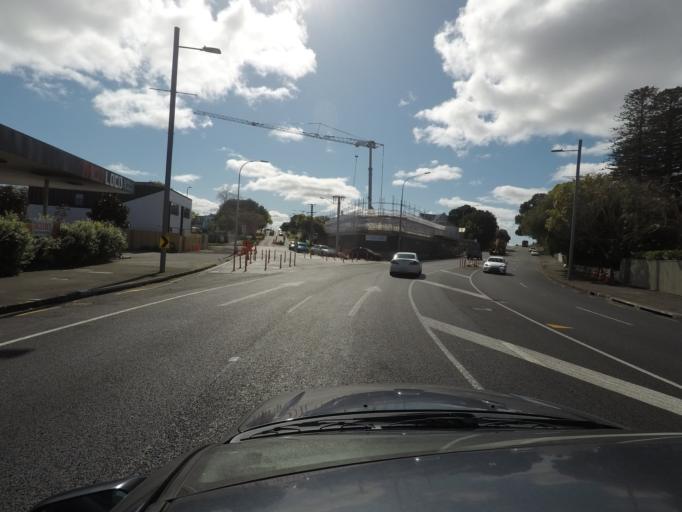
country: NZ
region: Auckland
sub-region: Auckland
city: Rosebank
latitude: -36.8824
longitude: 174.7176
